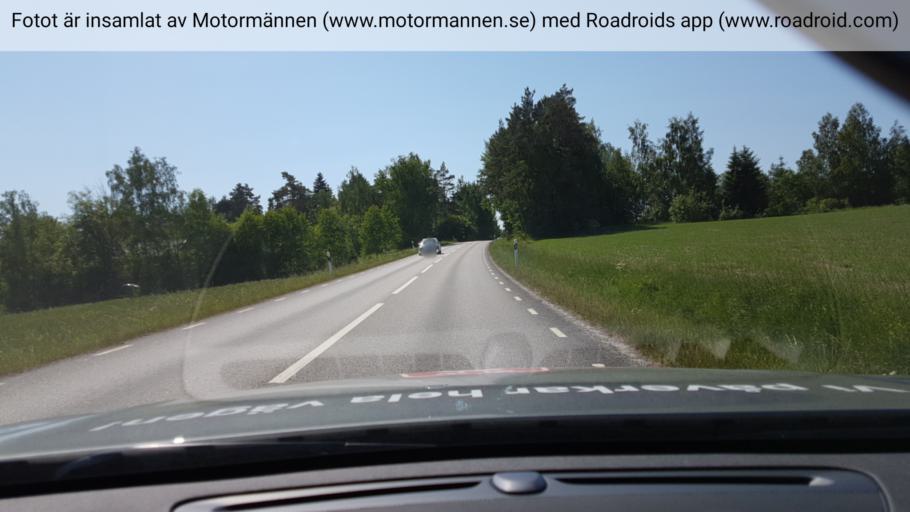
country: SE
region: Stockholm
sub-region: Norrtalje Kommun
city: Rimbo
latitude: 59.6796
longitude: 18.3633
